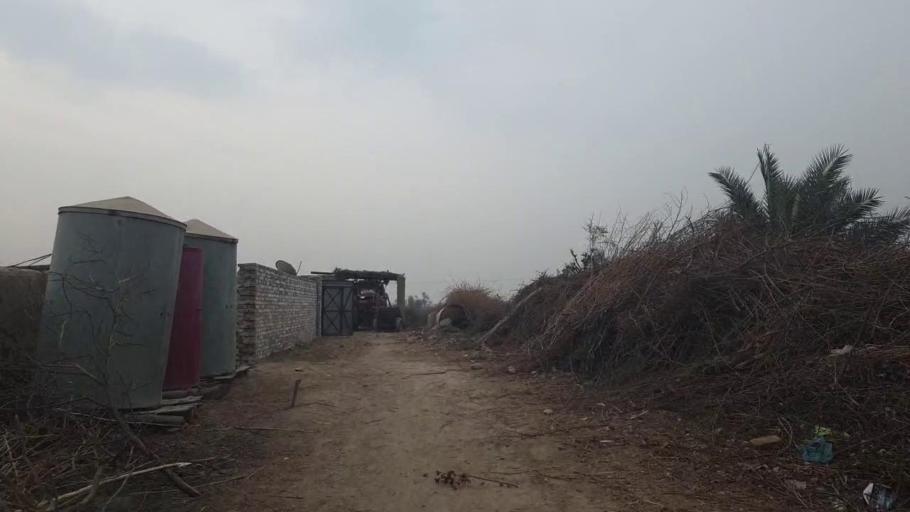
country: PK
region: Sindh
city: Tando Adam
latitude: 25.7378
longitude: 68.6880
